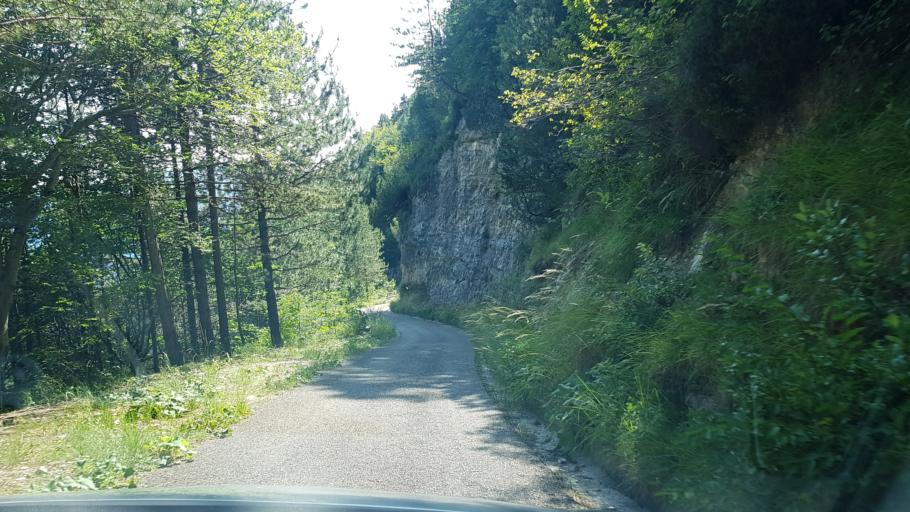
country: IT
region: Friuli Venezia Giulia
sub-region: Provincia di Udine
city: Moggio Udinese
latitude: 46.4495
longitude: 13.2168
